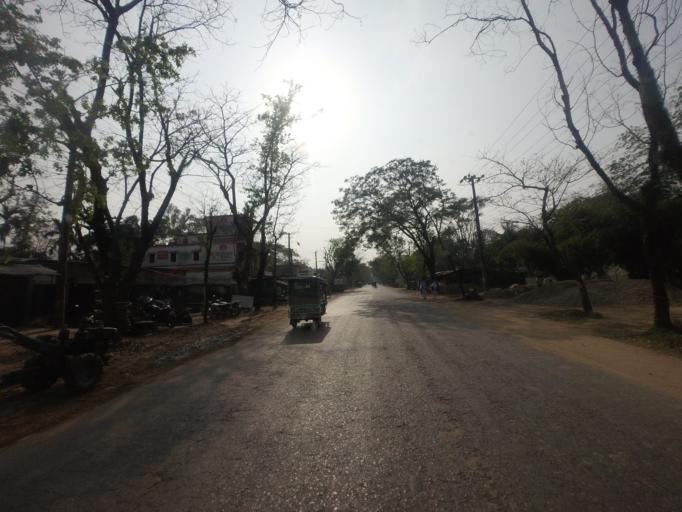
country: BD
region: Sylhet
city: Sylhet
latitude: 24.9141
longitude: 91.9407
